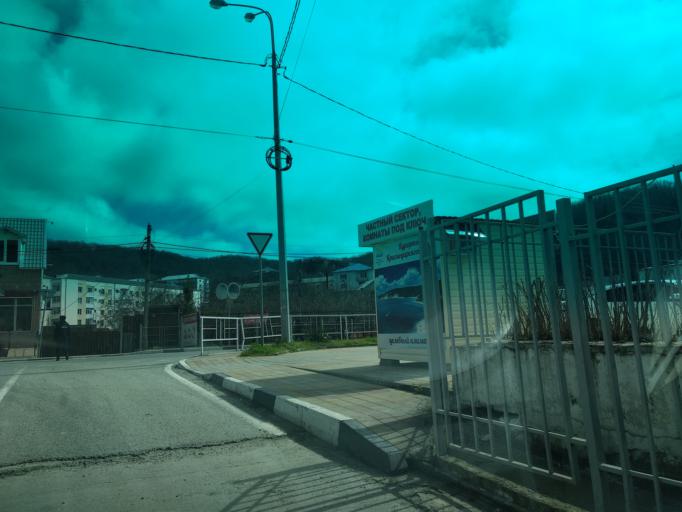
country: RU
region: Krasnodarskiy
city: Shepsi
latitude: 44.0411
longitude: 39.1505
